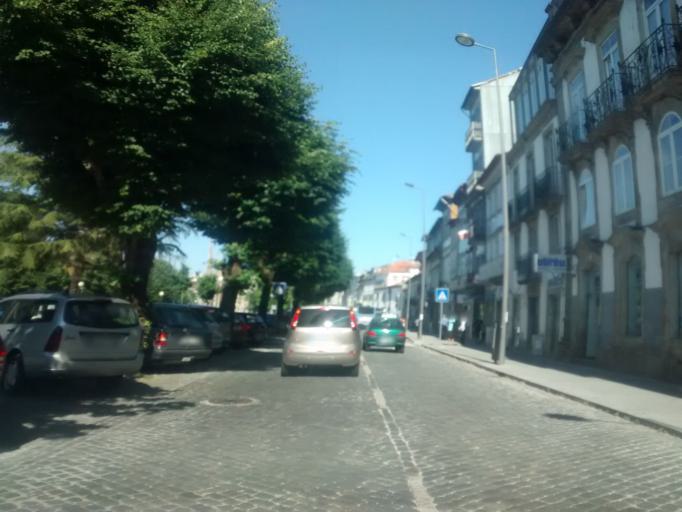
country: PT
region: Braga
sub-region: Braga
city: Braga
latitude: 41.5517
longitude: -8.4187
